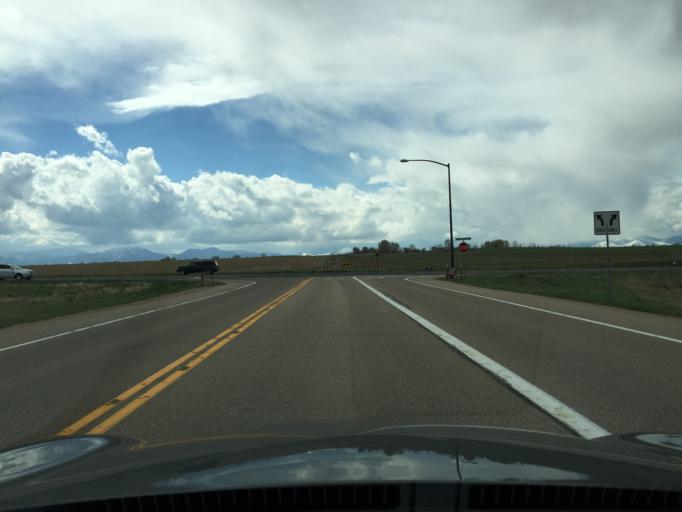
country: US
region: Colorado
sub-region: Boulder County
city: Erie
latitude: 40.0219
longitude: -105.0545
